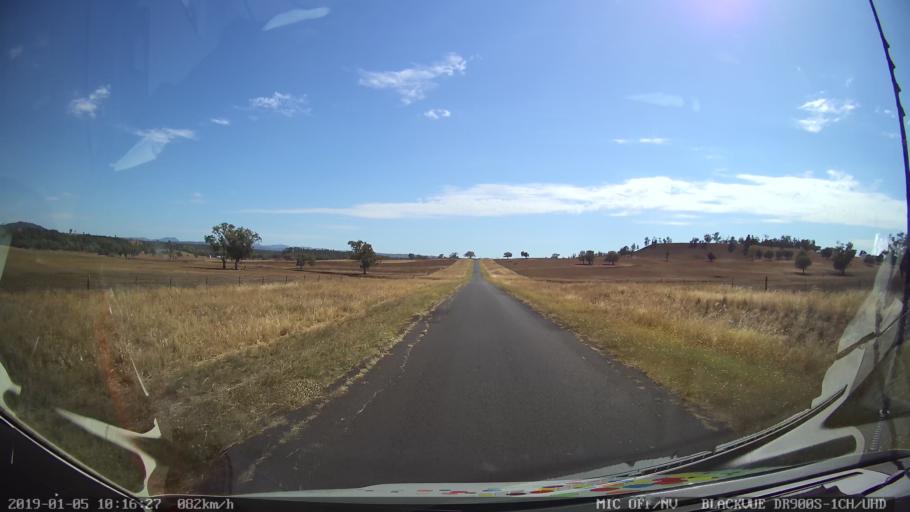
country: AU
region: New South Wales
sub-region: Gilgandra
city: Gilgandra
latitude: -31.5751
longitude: 148.9524
